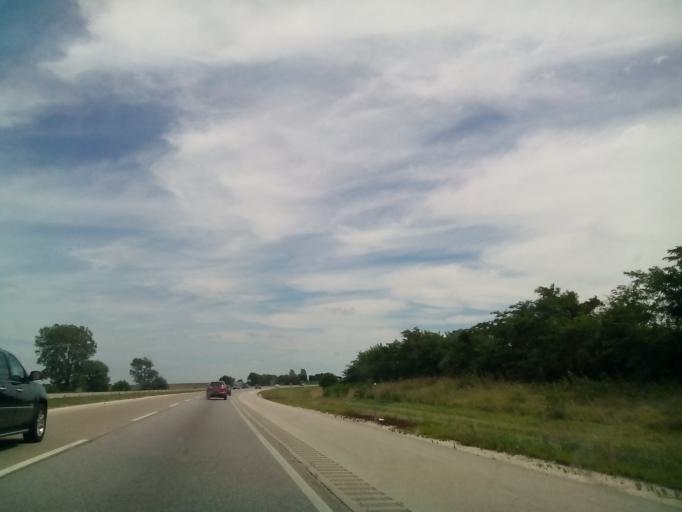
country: US
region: Illinois
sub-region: DeKalb County
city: Cortland
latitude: 41.9009
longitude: -88.6545
